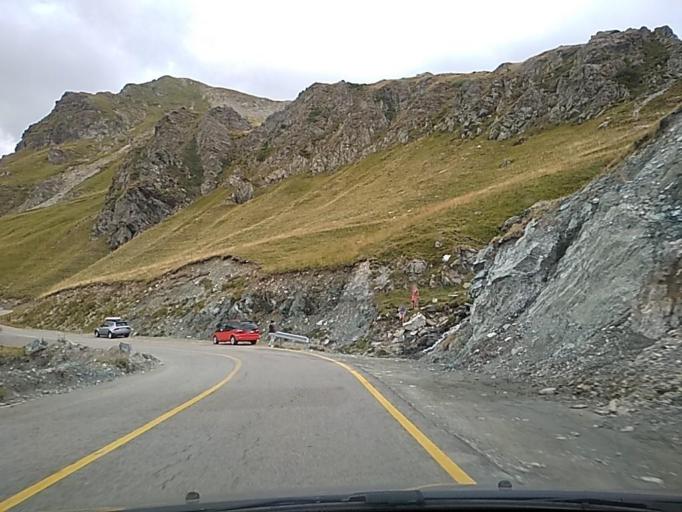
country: RO
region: Gorj
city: Novaci-Straini
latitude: 45.3584
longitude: 23.6533
